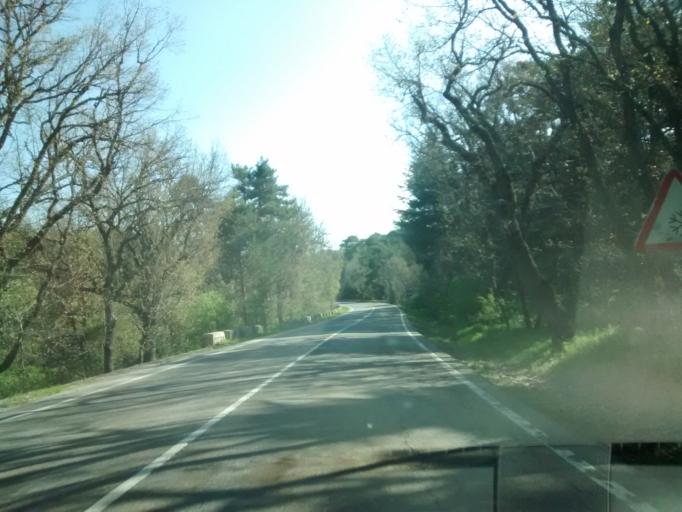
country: ES
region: Castille and Leon
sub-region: Provincia de Segovia
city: San Ildefonso
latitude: 40.8668
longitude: -4.0246
